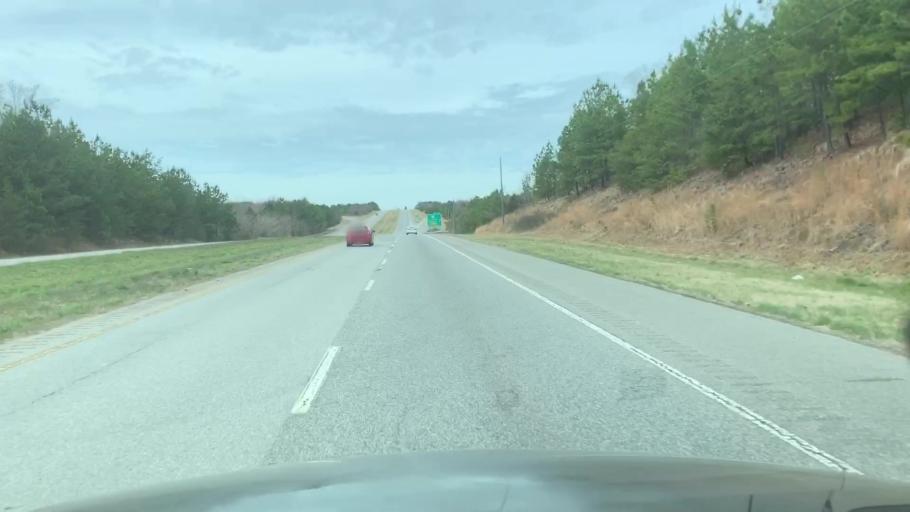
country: US
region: South Carolina
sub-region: Greenville County
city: Golden Grove
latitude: 34.7347
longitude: -82.4279
